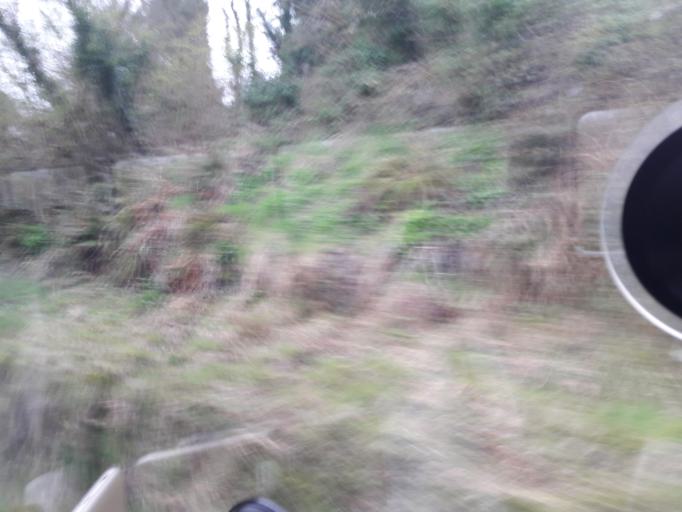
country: IE
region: Leinster
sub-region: An Longfort
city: Longford
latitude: 53.7249
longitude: -7.7713
